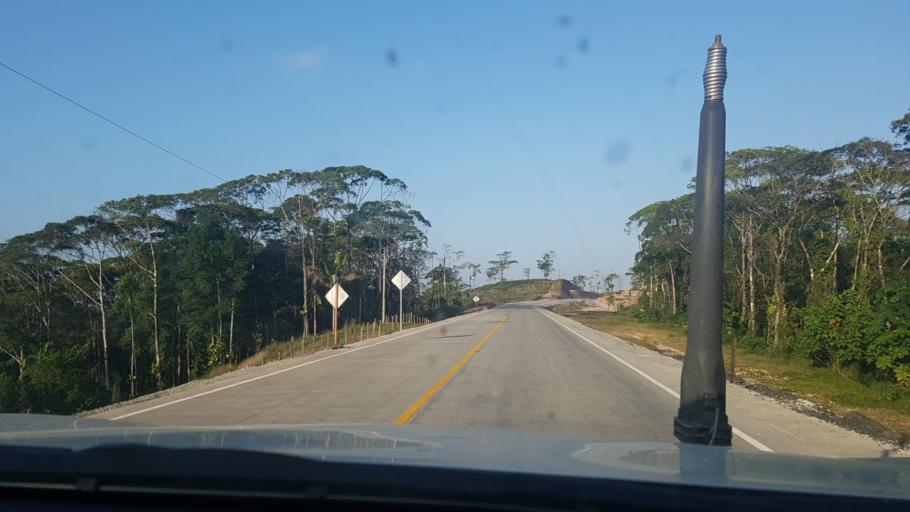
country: NI
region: Atlantico Sur
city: Rama
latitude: 11.8323
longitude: -84.0796
